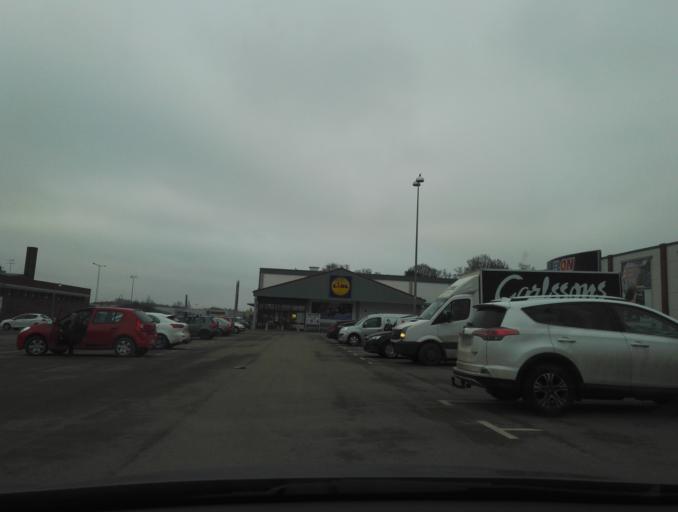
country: SE
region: Kronoberg
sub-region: Vaxjo Kommun
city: Vaexjoe
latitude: 56.8800
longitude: 14.7821
